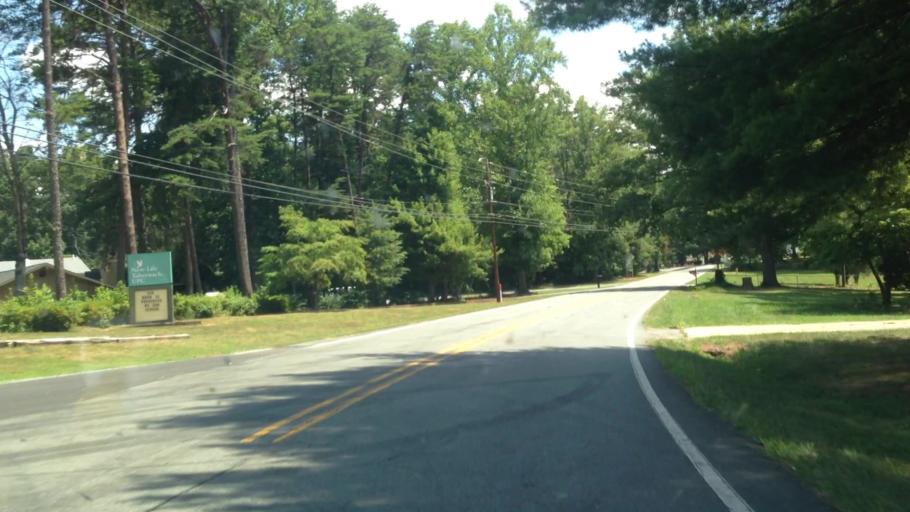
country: US
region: North Carolina
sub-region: Forsyth County
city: Kernersville
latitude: 36.1539
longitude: -80.0604
